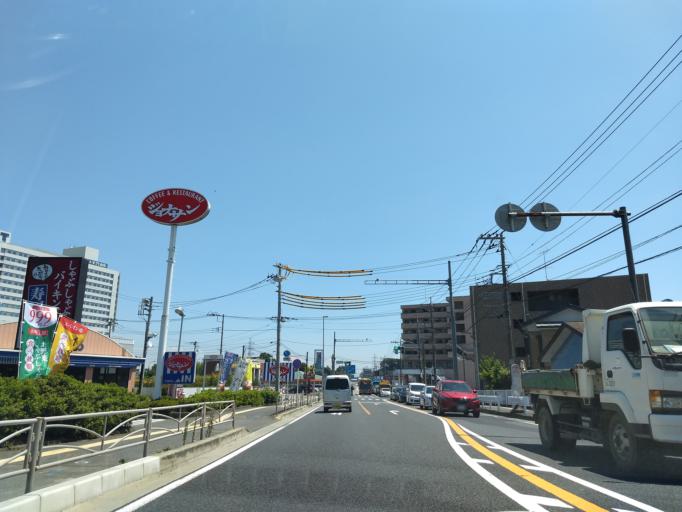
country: JP
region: Kanagawa
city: Isehara
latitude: 35.4042
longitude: 139.3135
